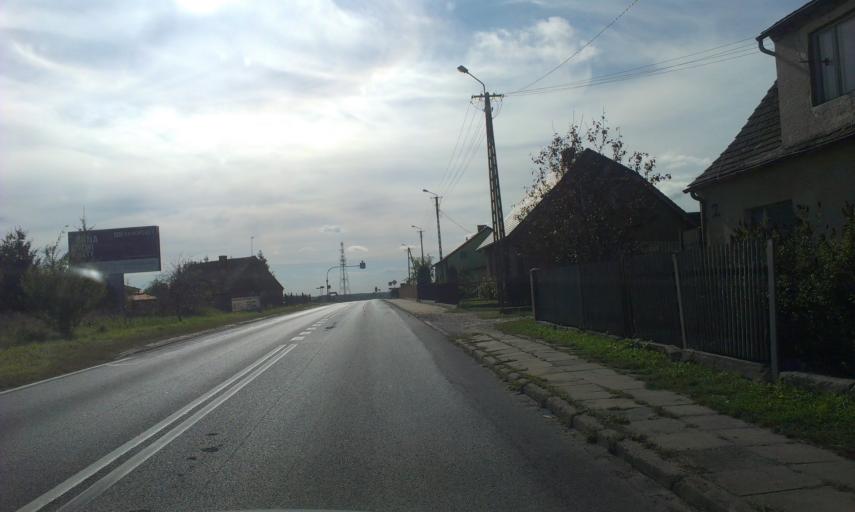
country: PL
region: Greater Poland Voivodeship
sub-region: Powiat zlotowski
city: Okonek
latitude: 53.6072
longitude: 16.7978
